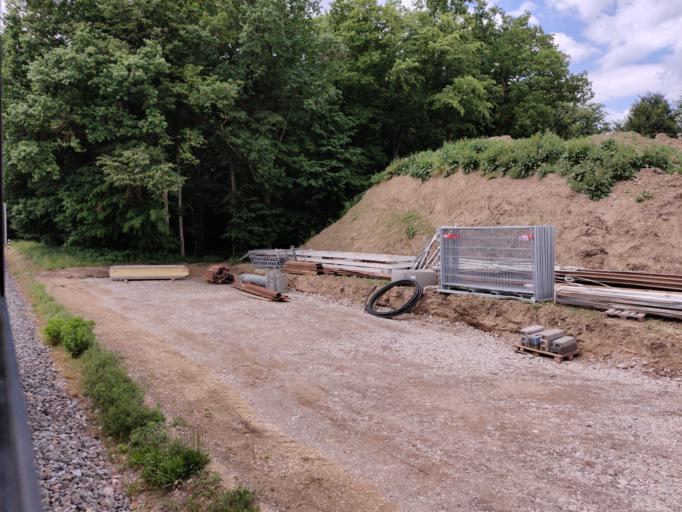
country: AT
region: Styria
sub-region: Politischer Bezirk Leibnitz
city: Spielfeld
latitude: 46.7187
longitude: 15.6537
